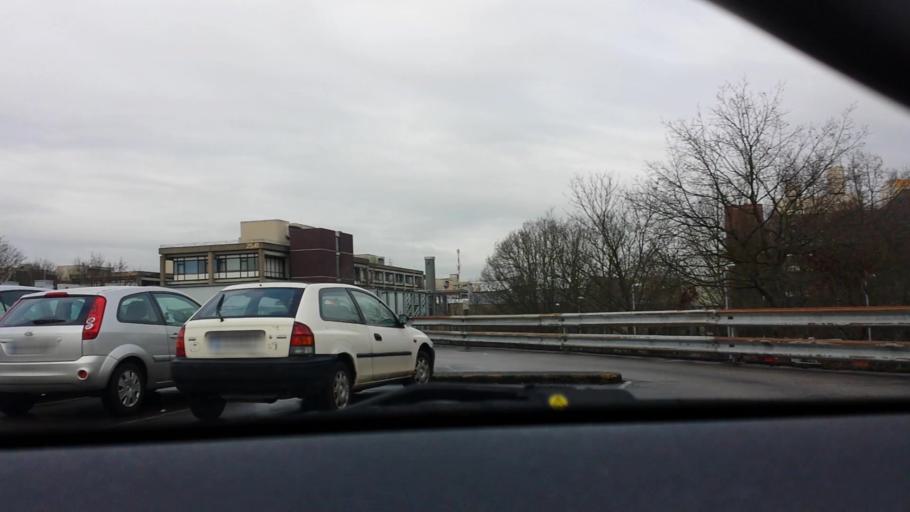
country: DE
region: North Rhine-Westphalia
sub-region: Regierungsbezirk Dusseldorf
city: Dusseldorf
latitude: 51.1857
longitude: 6.7989
